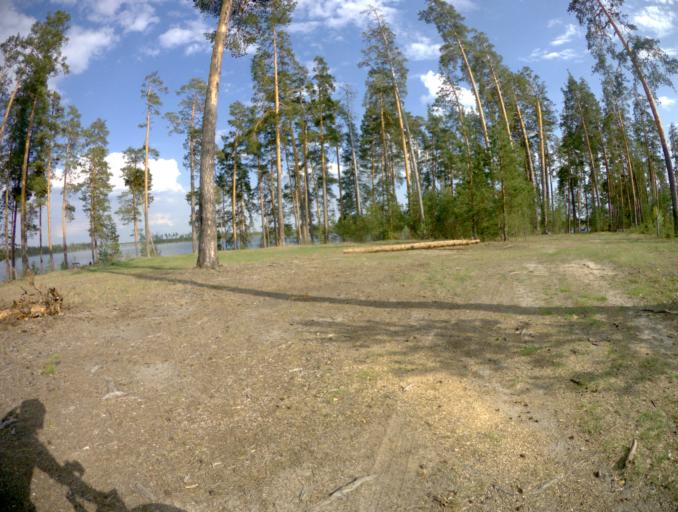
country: RU
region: Ivanovo
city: Talitsy
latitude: 56.4156
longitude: 42.2773
